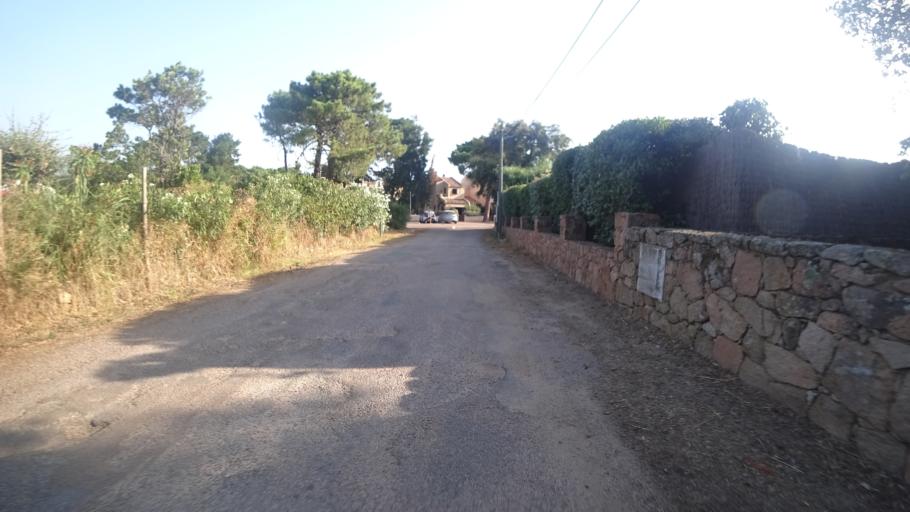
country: FR
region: Corsica
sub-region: Departement de la Corse-du-Sud
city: Porto-Vecchio
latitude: 41.6376
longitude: 9.3417
